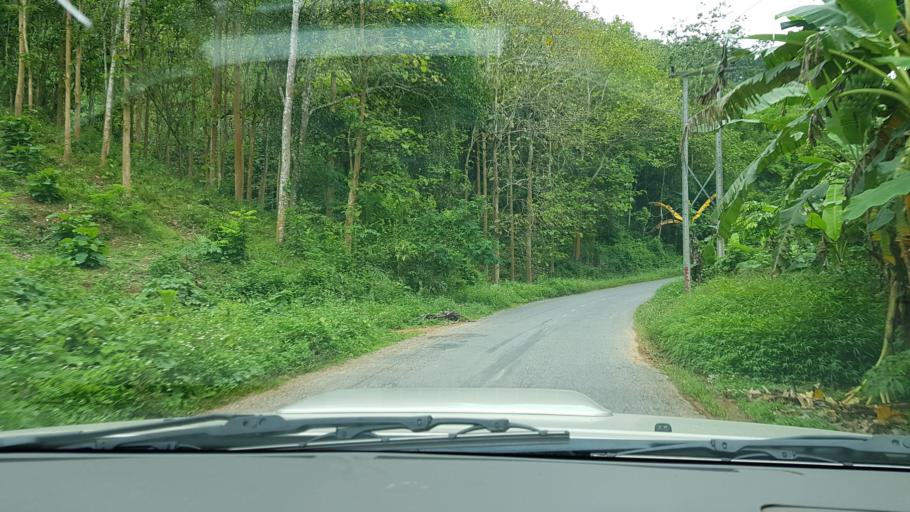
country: LA
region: Phongsali
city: Khoa
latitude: 21.0602
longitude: 102.3868
